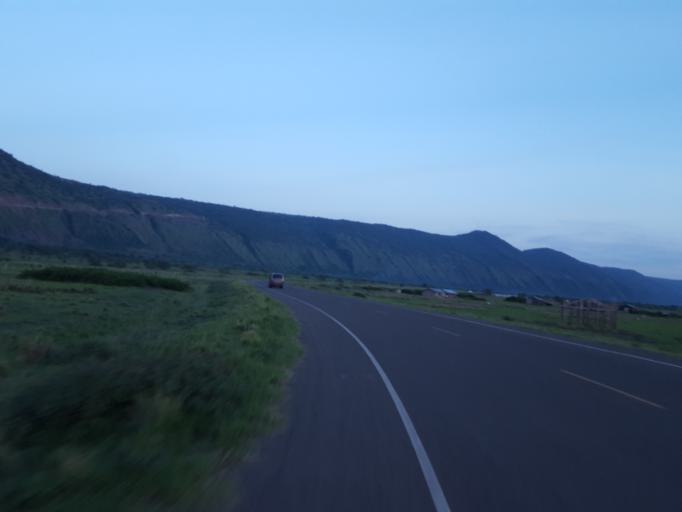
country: UG
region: Western Region
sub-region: Kibale District
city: Kagadi
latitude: 1.2524
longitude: 30.7483
